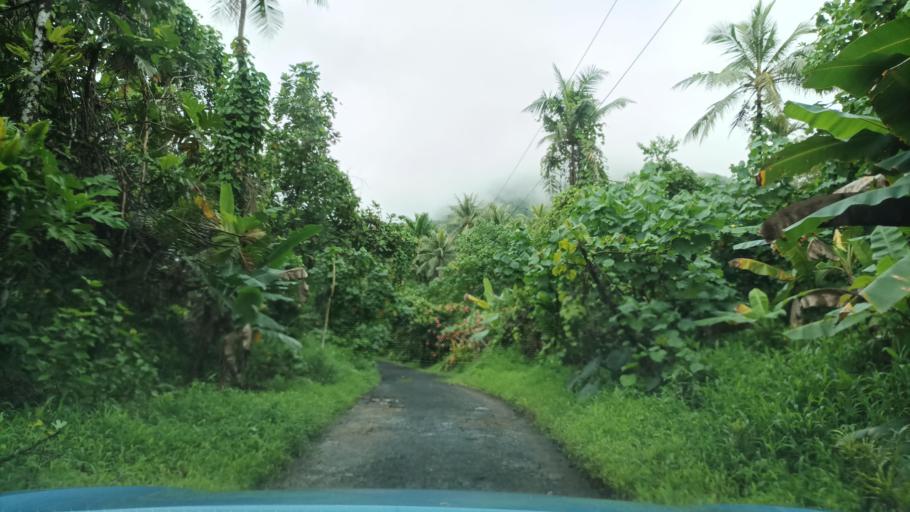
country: FM
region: Pohnpei
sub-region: Kolonia Municipality
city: Kolonia
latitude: 6.9201
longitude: 158.2749
